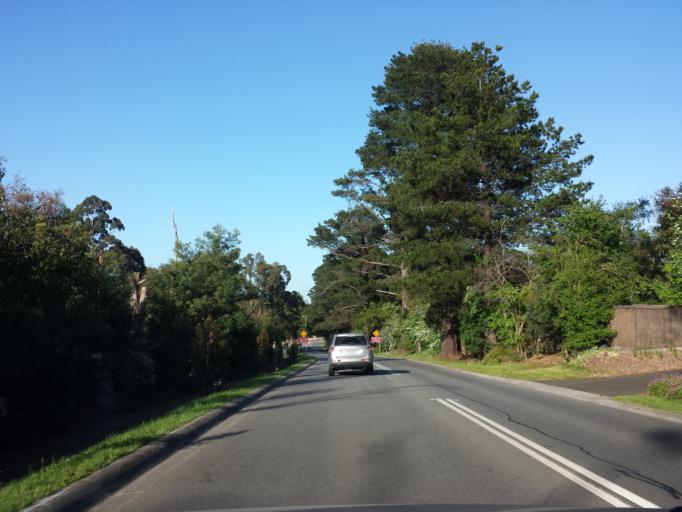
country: AU
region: Victoria
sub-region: Casey
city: Narre Warren North
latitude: -37.9986
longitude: 145.3439
